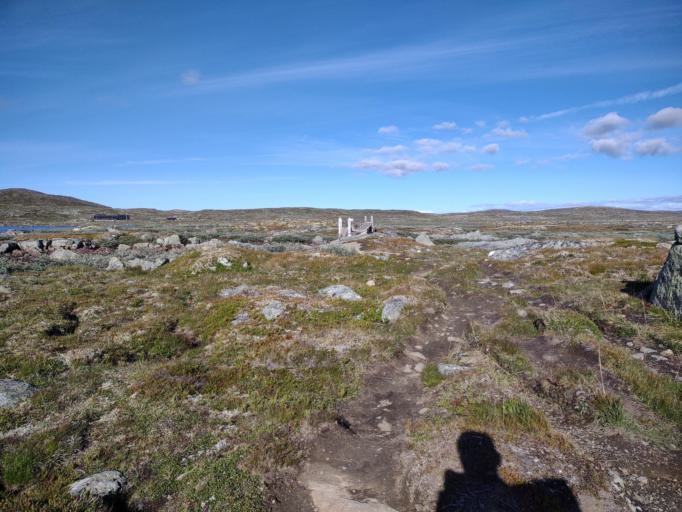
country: NO
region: Hordaland
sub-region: Eidfjord
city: Eidfjord
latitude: 60.1779
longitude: 7.4725
